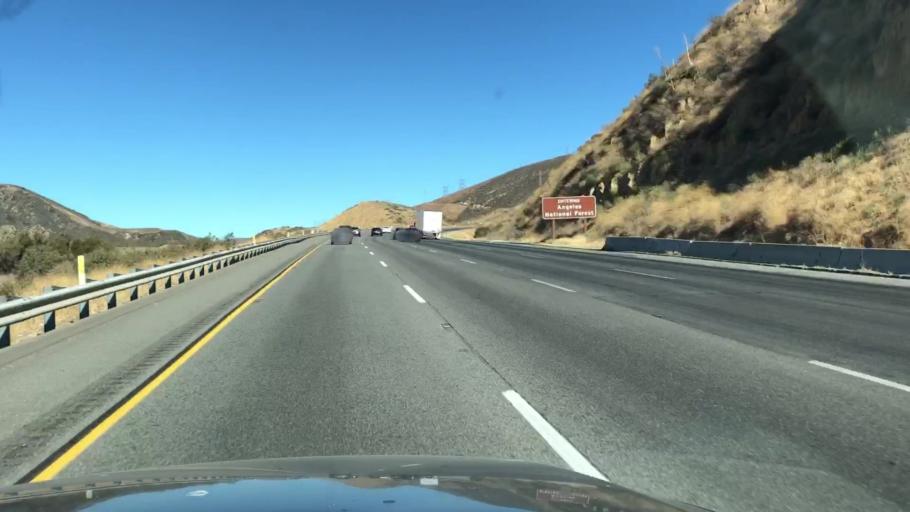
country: US
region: California
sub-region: Los Angeles County
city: Castaic
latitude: 34.5500
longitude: -118.6703
